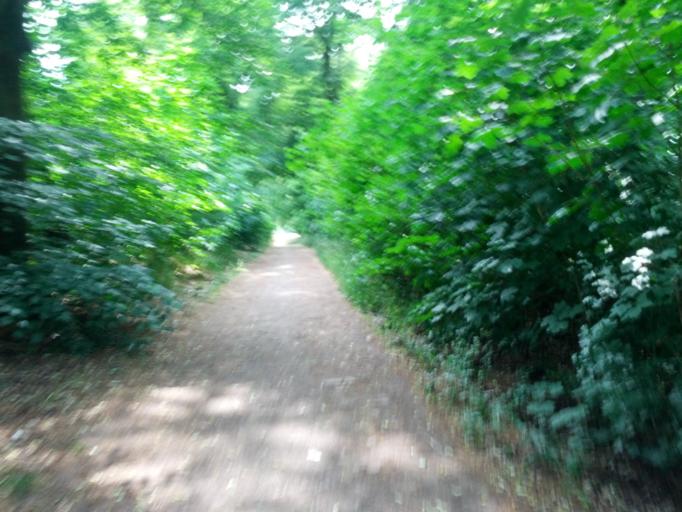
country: DE
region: Thuringia
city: Eisenach
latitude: 50.9663
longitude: 10.3318
